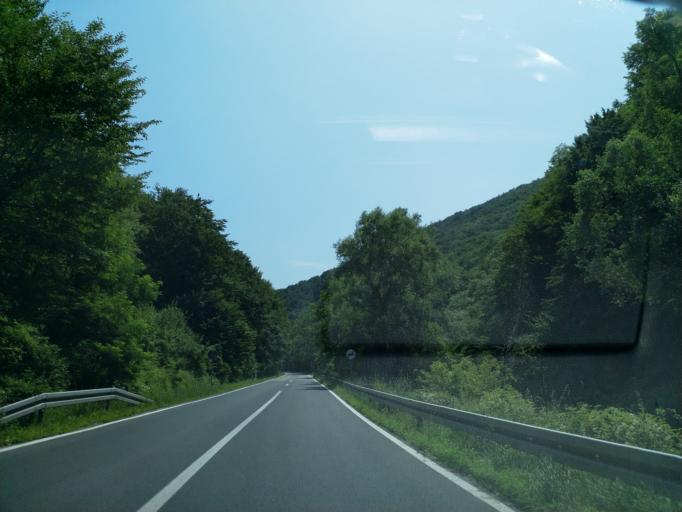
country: RS
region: Central Serbia
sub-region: Toplicki Okrug
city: Blace
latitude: 43.3361
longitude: 21.2058
